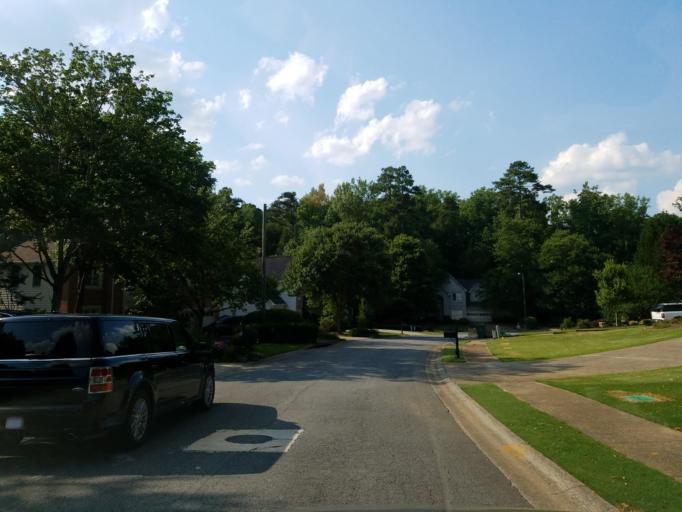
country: US
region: Georgia
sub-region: Cobb County
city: Marietta
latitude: 33.9471
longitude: -84.4826
